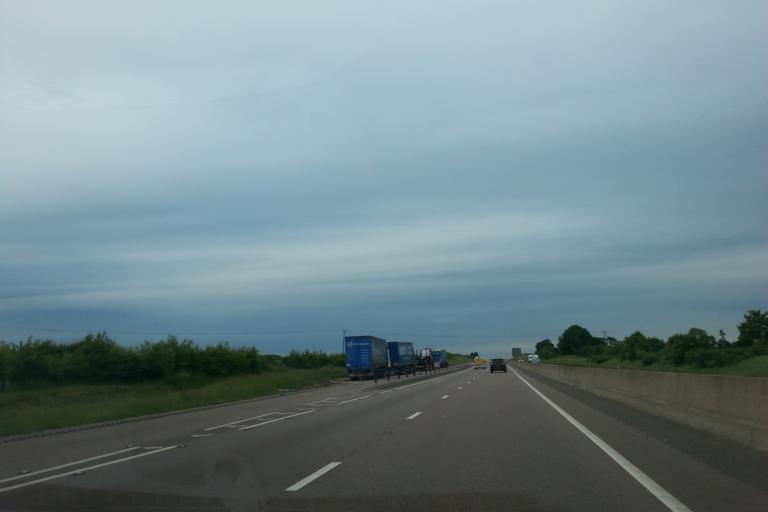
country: GB
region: England
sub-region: Nottinghamshire
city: East Bridgford
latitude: 52.9864
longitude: -0.9367
